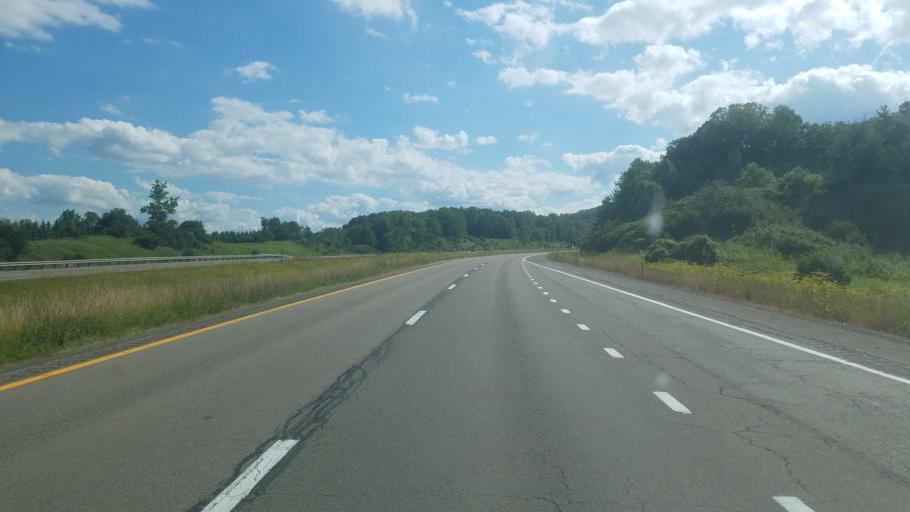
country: US
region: New York
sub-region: Allegany County
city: Alfred
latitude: 42.3203
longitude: -77.7455
